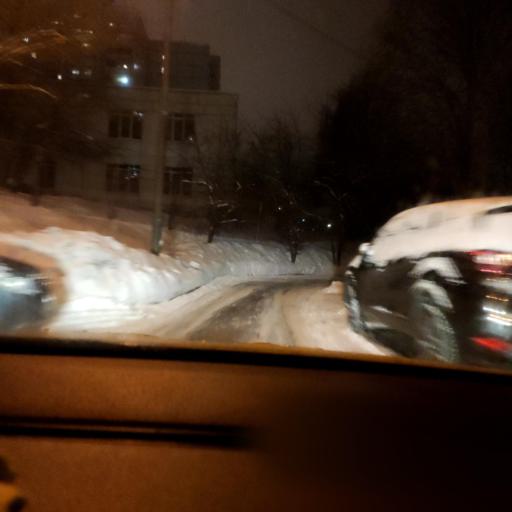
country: RU
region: Moscow
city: Yasenevo
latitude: 55.5904
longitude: 37.5480
